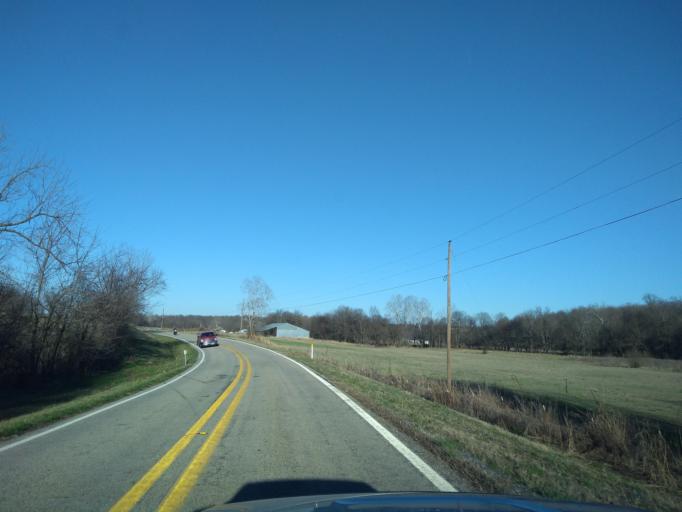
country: US
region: Arkansas
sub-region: Washington County
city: Farmington
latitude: 36.0952
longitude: -94.3550
